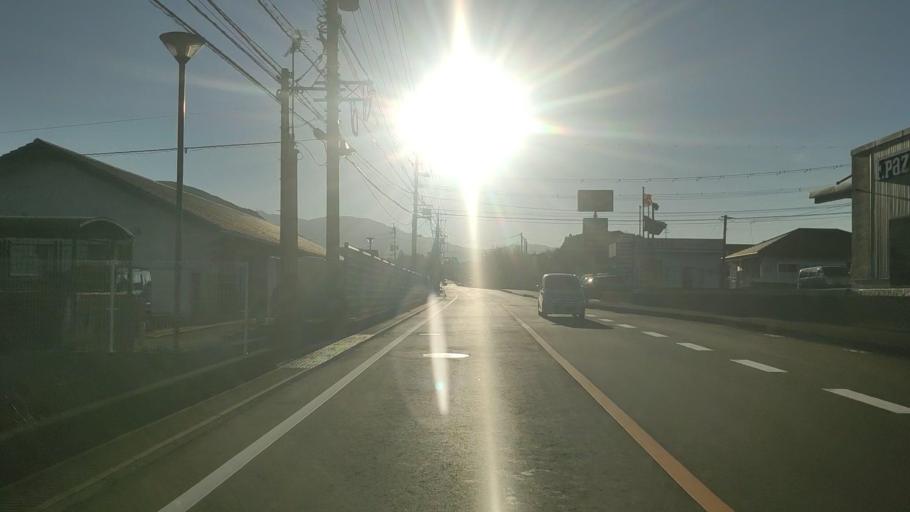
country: JP
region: Miyazaki
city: Miyazaki-shi
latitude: 31.8449
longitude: 131.3443
